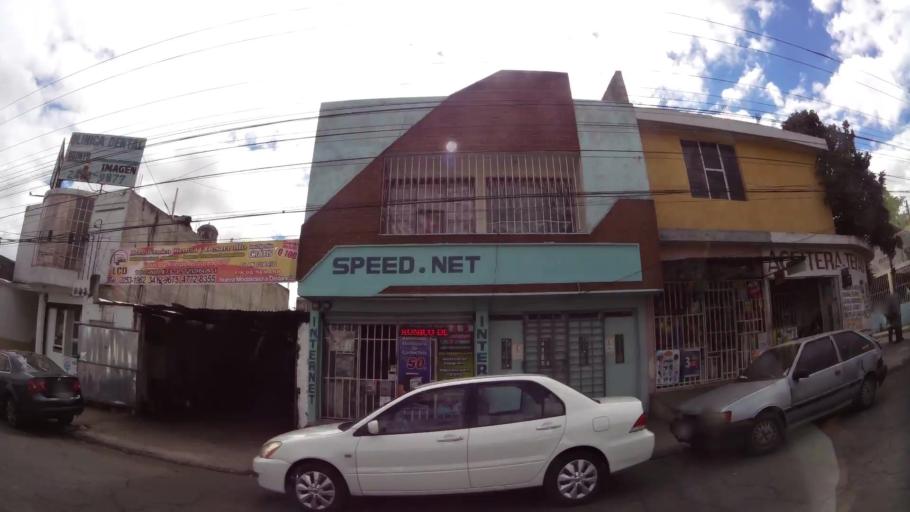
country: GT
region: Guatemala
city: Guatemala City
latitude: 14.6817
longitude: -90.5478
